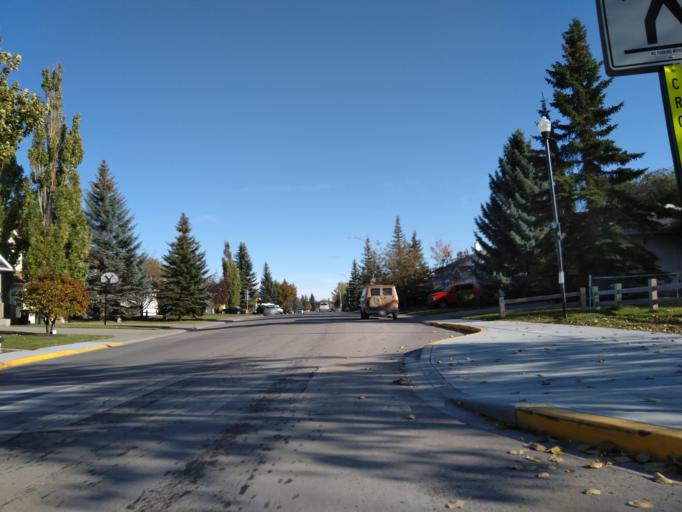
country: CA
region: Alberta
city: Cochrane
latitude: 51.1799
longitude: -114.4779
